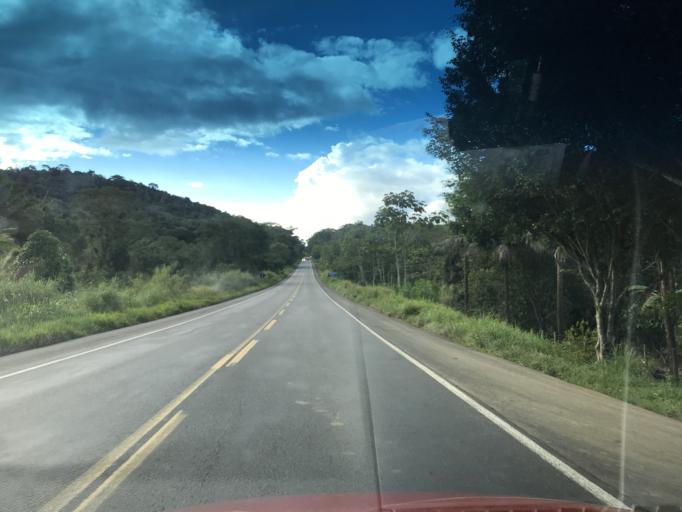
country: BR
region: Bahia
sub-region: Ibirapitanga
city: Ibirapitanga
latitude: -14.1969
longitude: -39.3139
